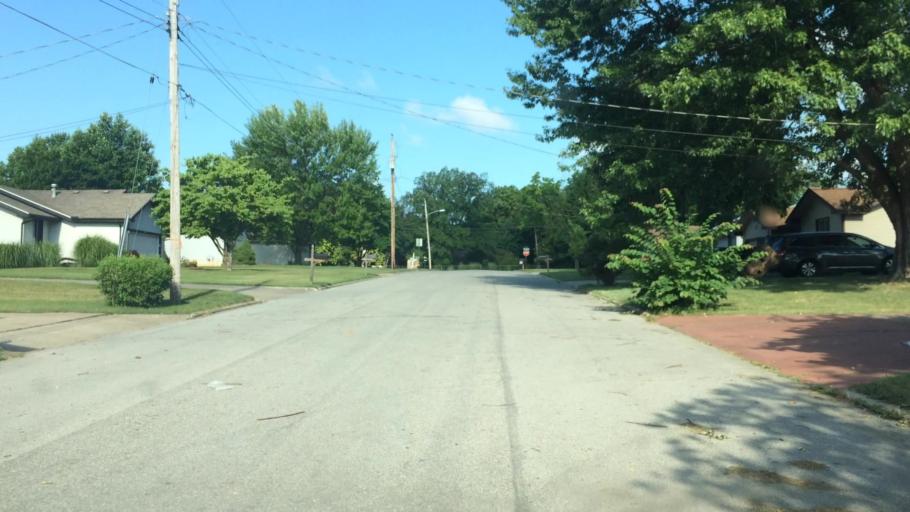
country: US
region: Missouri
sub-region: Greene County
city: Springfield
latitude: 37.2606
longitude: -93.2794
